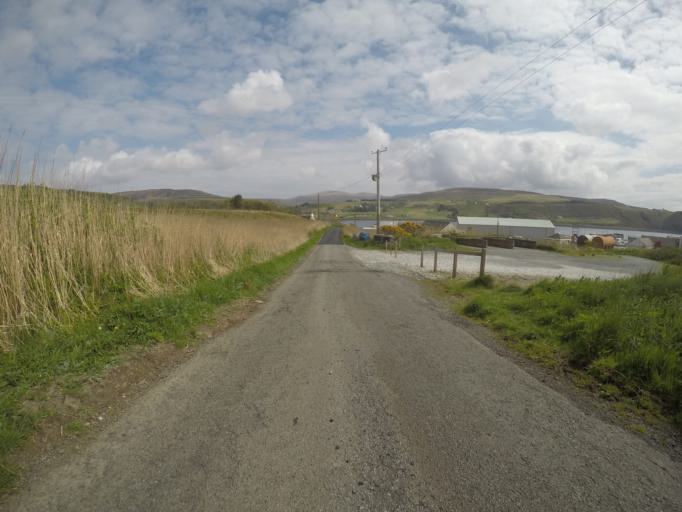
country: GB
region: Scotland
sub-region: Highland
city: Portree
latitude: 57.5879
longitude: -6.3788
